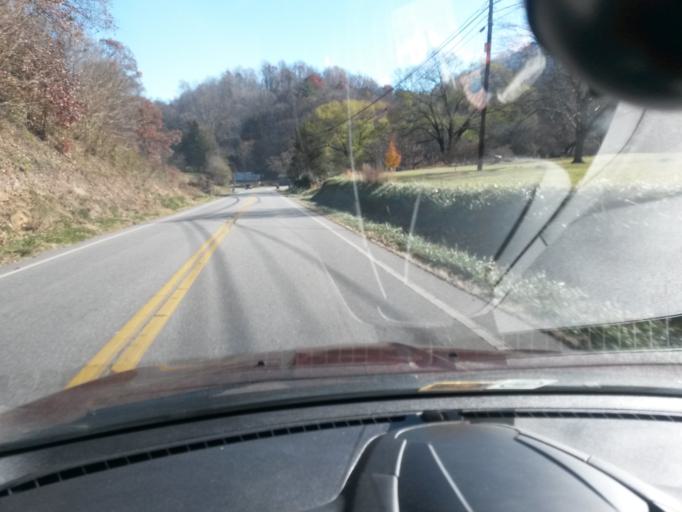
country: US
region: Virginia
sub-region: Henry County
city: Bassett
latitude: 36.7614
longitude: -80.0111
